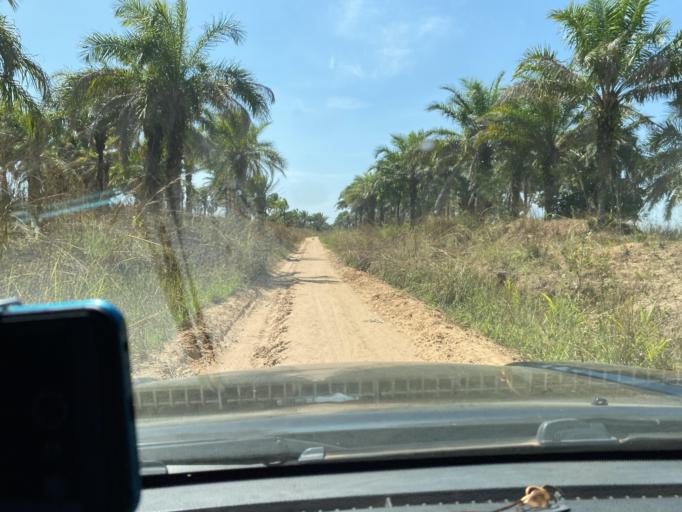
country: CD
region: Kasai-Oriental
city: Kabinda
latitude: -5.8881
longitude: 24.8474
